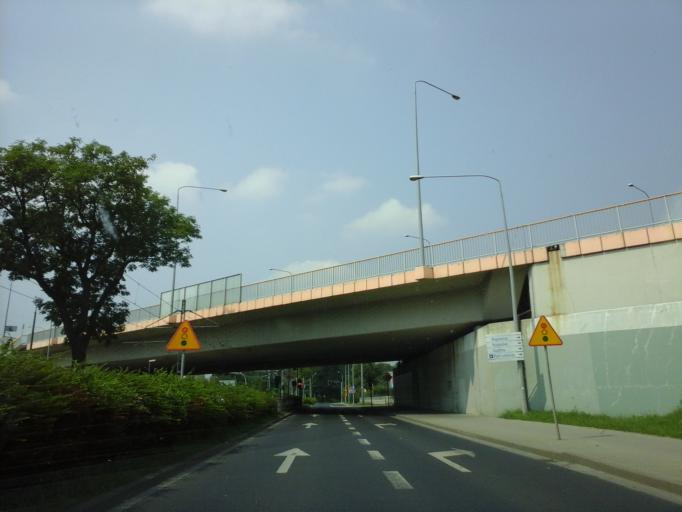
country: PL
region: Lower Silesian Voivodeship
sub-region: Powiat wroclawski
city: Wroclaw
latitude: 51.1359
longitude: 16.9995
